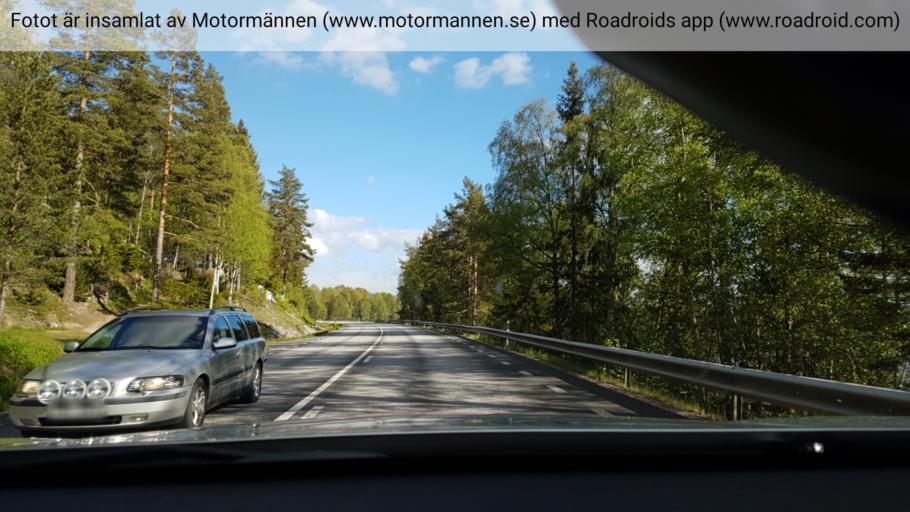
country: SE
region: Dalarna
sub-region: Faluns Kommun
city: Bjursas
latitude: 60.7617
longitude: 15.3227
